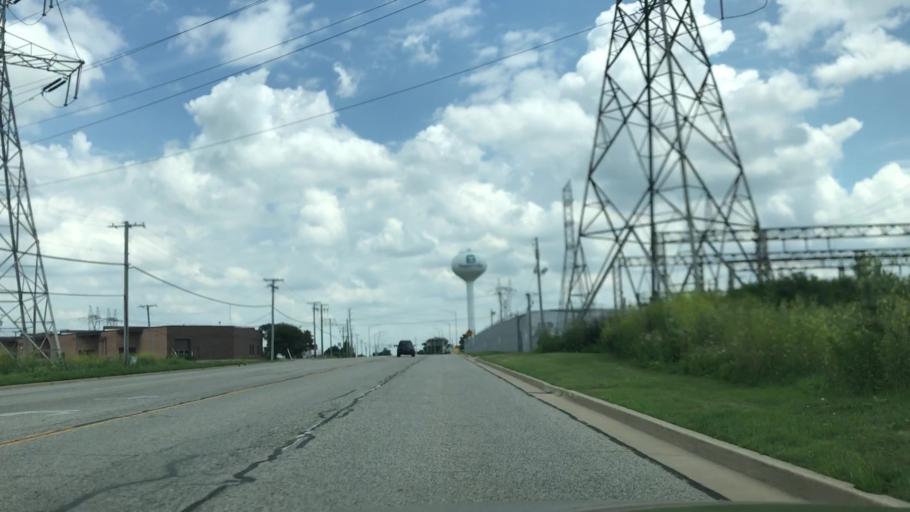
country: US
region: Illinois
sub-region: DuPage County
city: Warrenville
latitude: 41.7992
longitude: -88.2341
